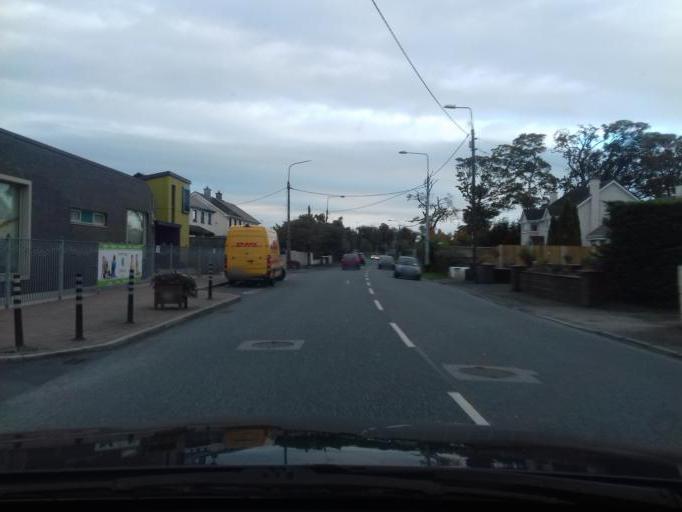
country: IE
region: Leinster
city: Hartstown
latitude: 53.4103
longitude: -6.4373
